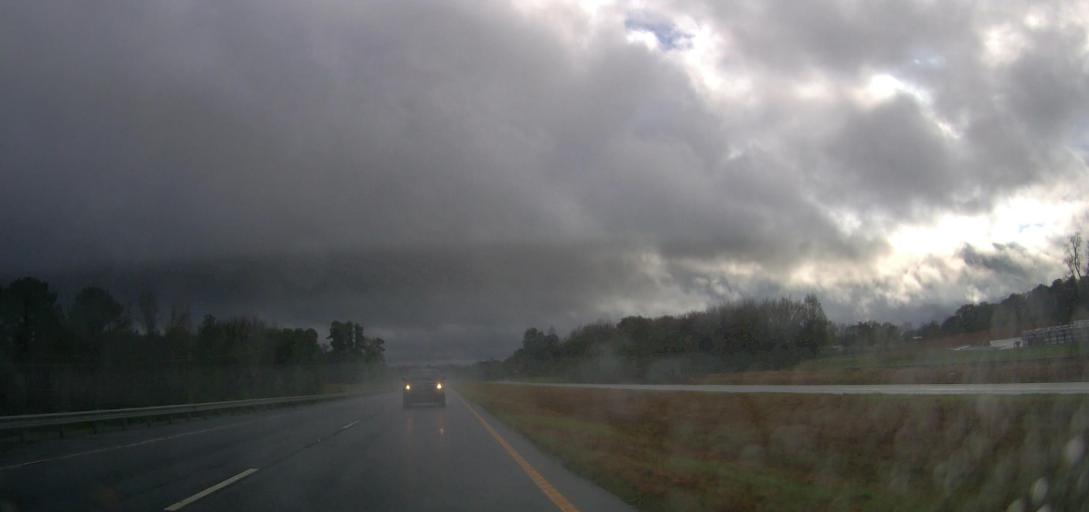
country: US
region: Georgia
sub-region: Clarke County
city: Country Club Estates
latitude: 34.0365
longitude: -83.4021
